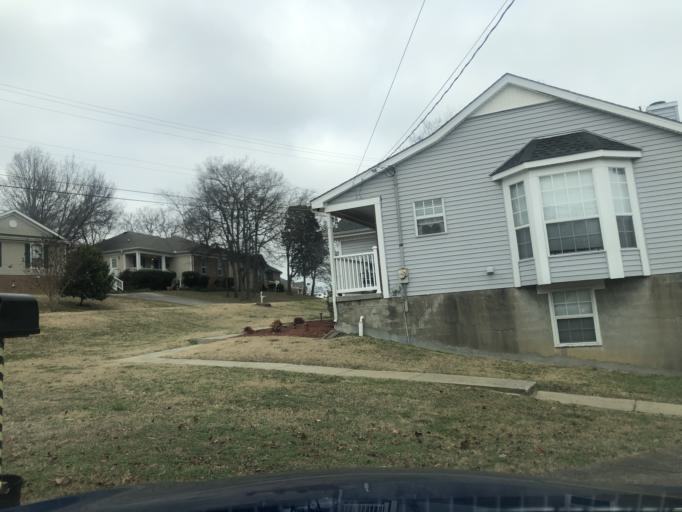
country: US
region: Tennessee
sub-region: Davidson County
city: Oak Hill
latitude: 36.0878
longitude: -86.7047
